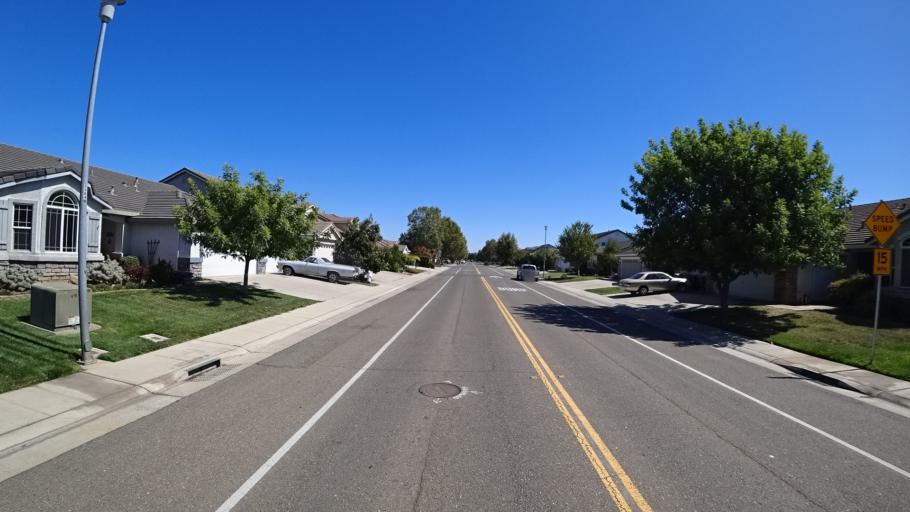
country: US
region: California
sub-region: Sacramento County
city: Elk Grove
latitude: 38.4022
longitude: -121.3472
